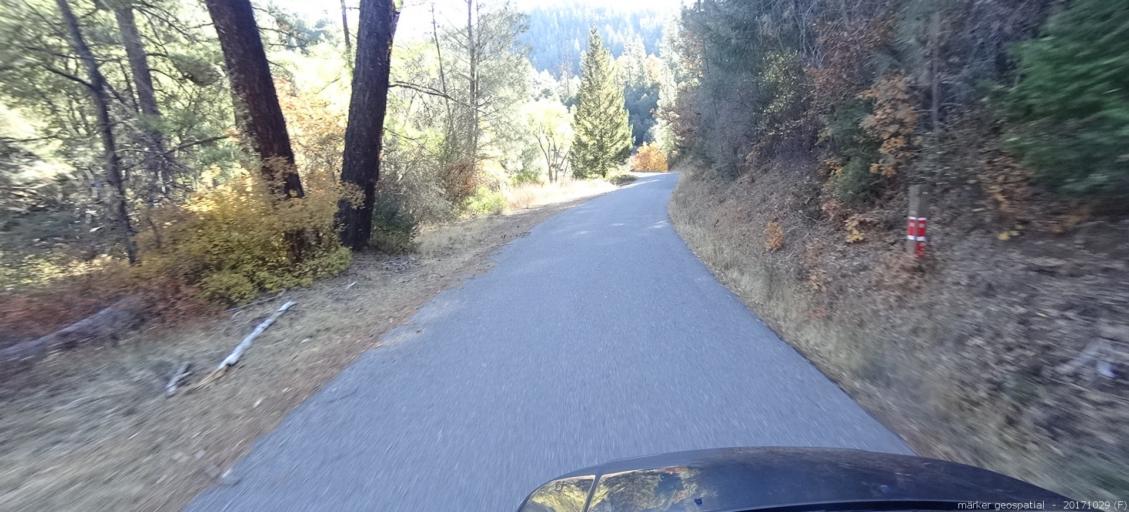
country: US
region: California
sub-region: Trinity County
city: Hayfork
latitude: 40.3828
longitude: -122.9814
